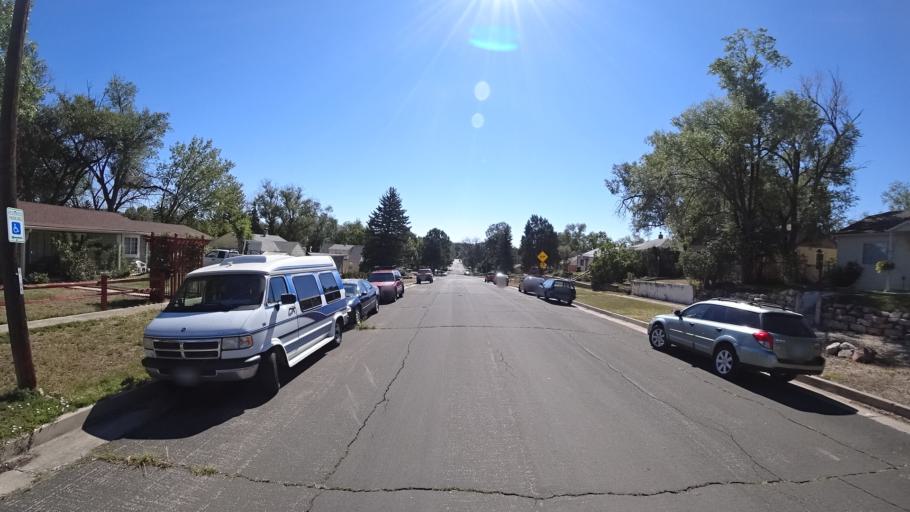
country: US
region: Colorado
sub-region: El Paso County
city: Colorado Springs
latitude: 38.8451
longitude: -104.8501
